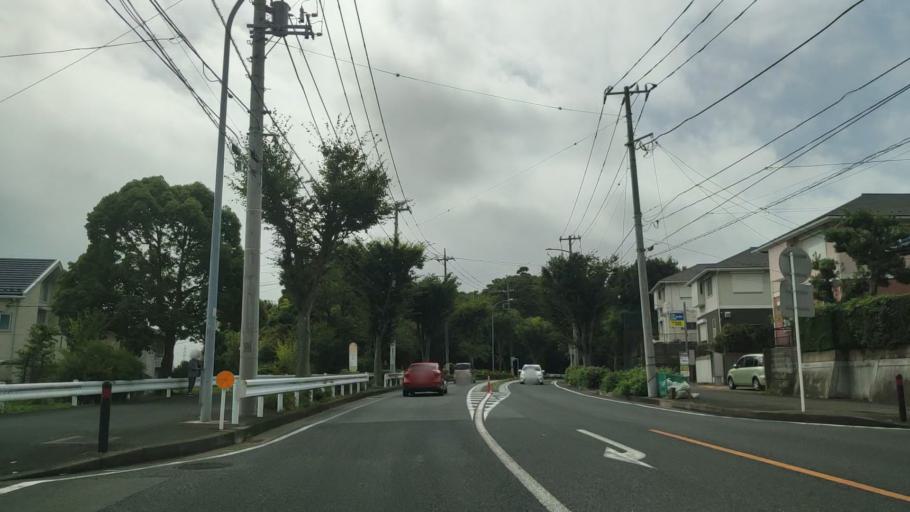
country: JP
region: Kanagawa
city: Fujisawa
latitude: 35.4100
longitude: 139.5212
